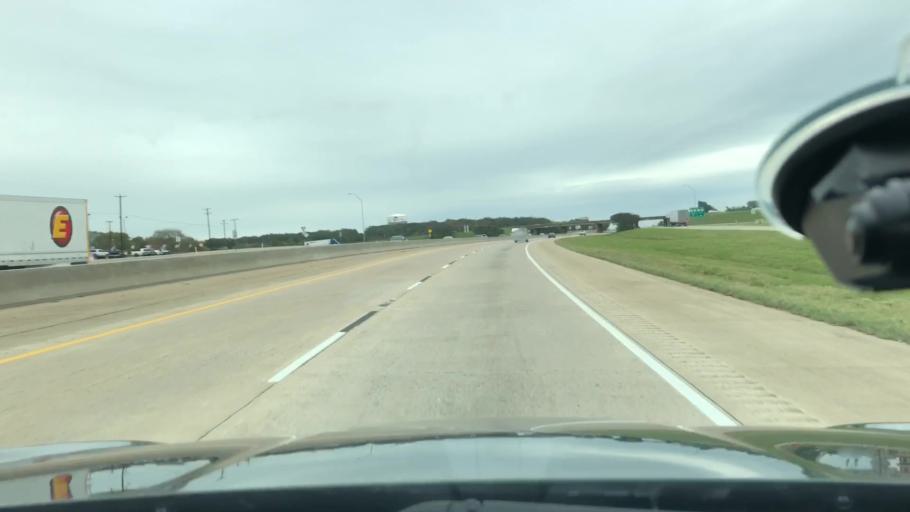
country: US
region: Texas
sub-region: Hopkins County
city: Sulphur Springs
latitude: 33.1207
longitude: -95.6393
